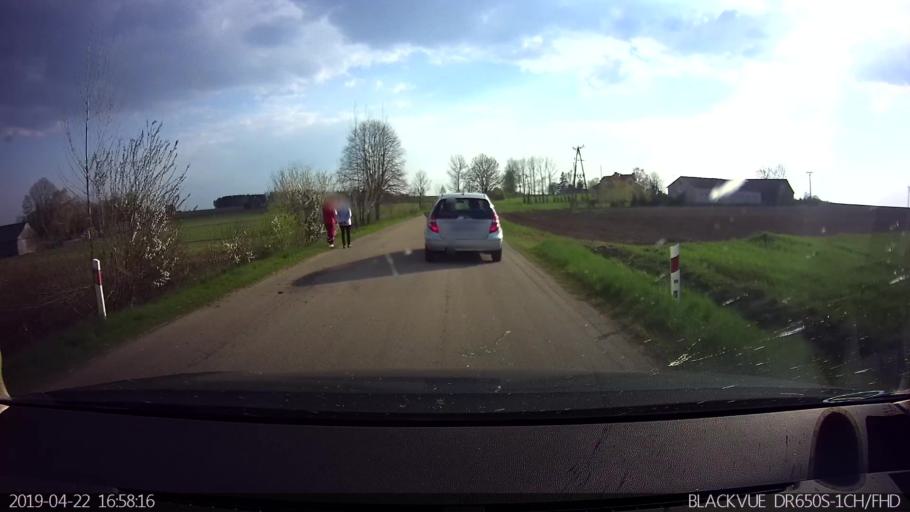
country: PL
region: Podlasie
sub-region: Powiat siemiatycki
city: Siemiatycze
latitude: 52.4727
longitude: 22.7529
